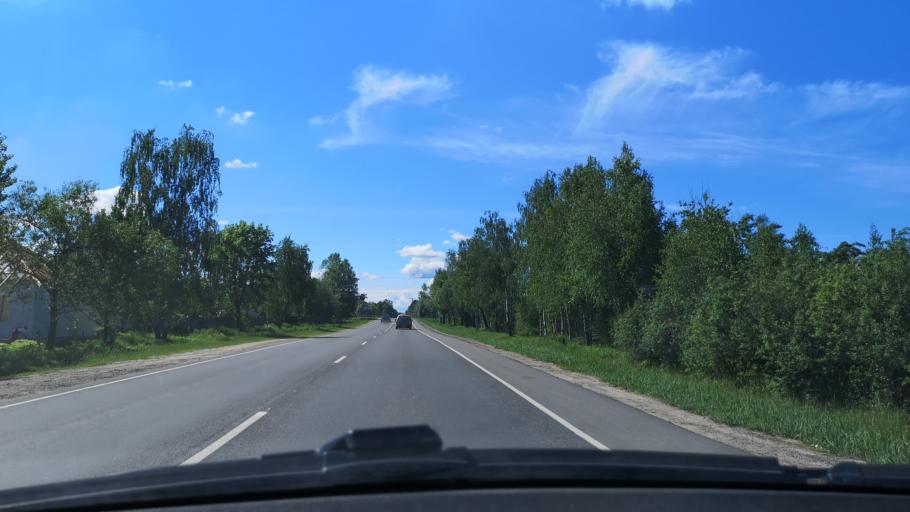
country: BY
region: Brest
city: Brest
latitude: 52.0436
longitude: 23.7277
